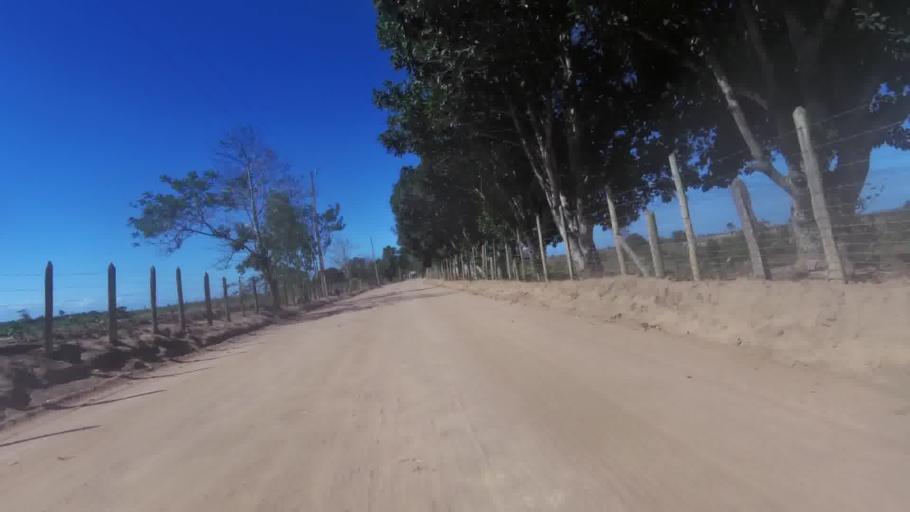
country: BR
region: Espirito Santo
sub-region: Marataizes
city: Marataizes
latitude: -21.1349
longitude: -40.9906
